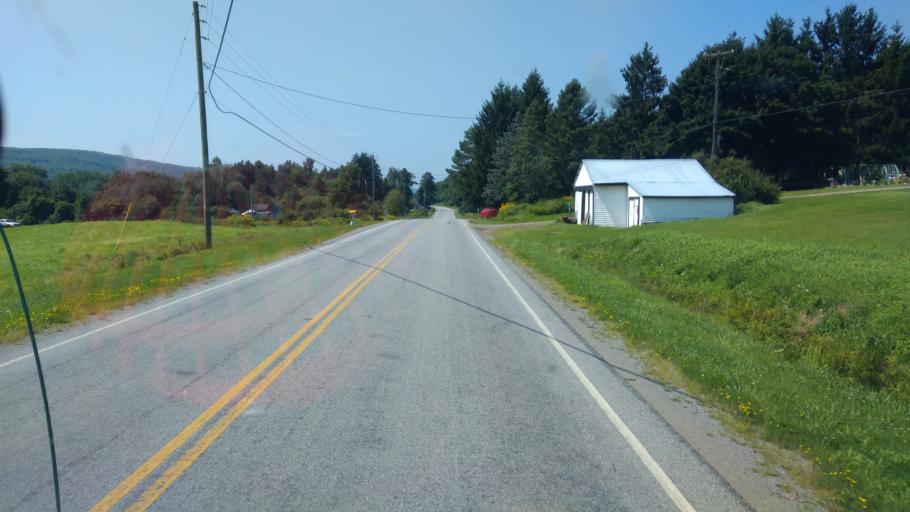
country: US
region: New York
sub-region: Allegany County
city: Belmont
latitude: 42.3028
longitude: -77.9788
